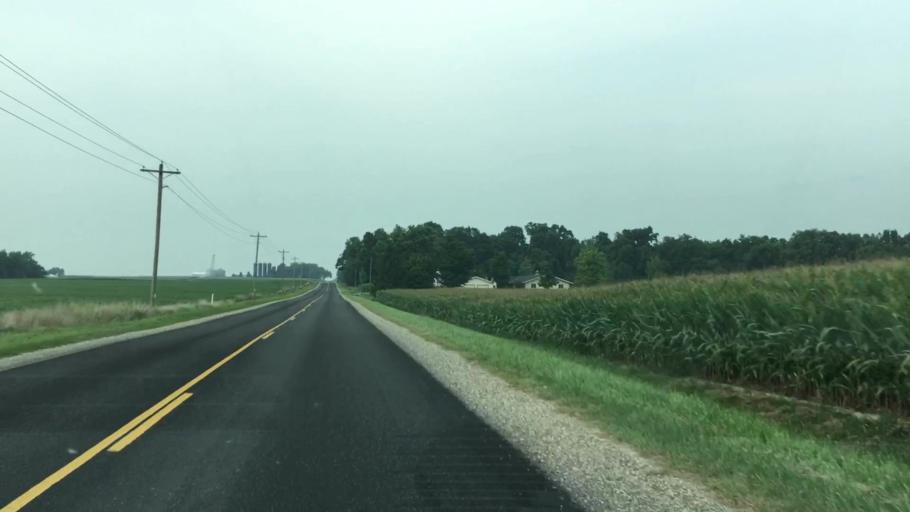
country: US
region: Michigan
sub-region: Ottawa County
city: Hudsonville
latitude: 42.7852
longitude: -85.9010
